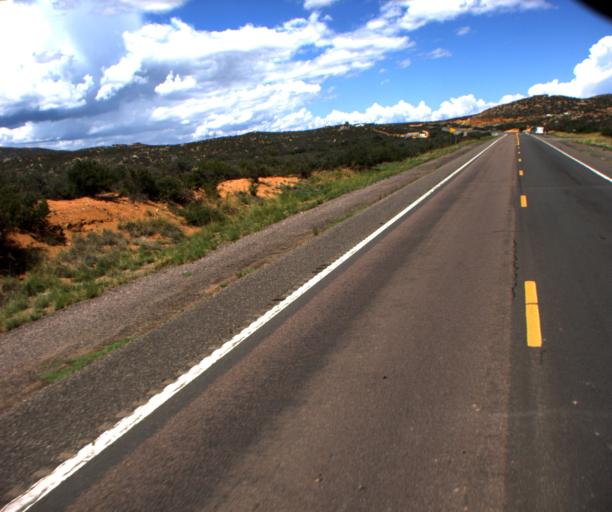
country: US
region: Arizona
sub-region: Yavapai County
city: Dewey-Humboldt
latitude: 34.5435
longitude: -112.1547
